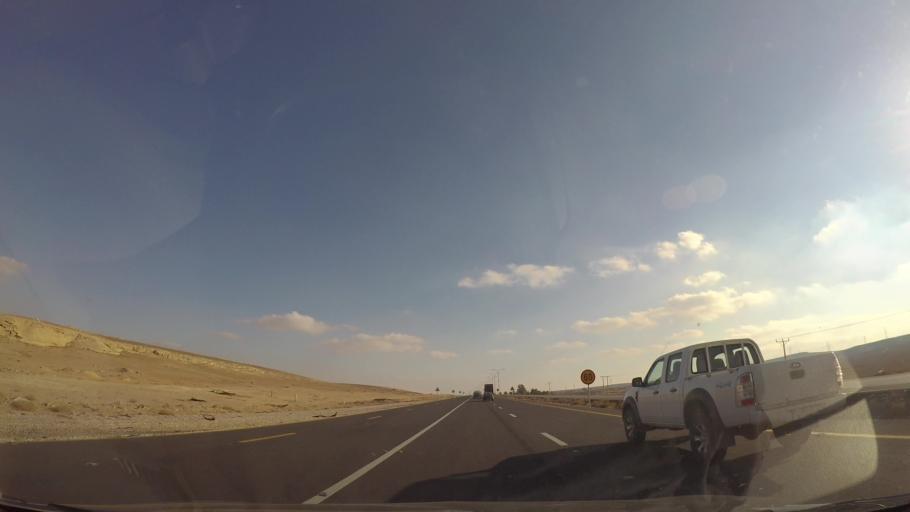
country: JO
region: Karak
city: Karak City
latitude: 31.1055
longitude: 36.0071
